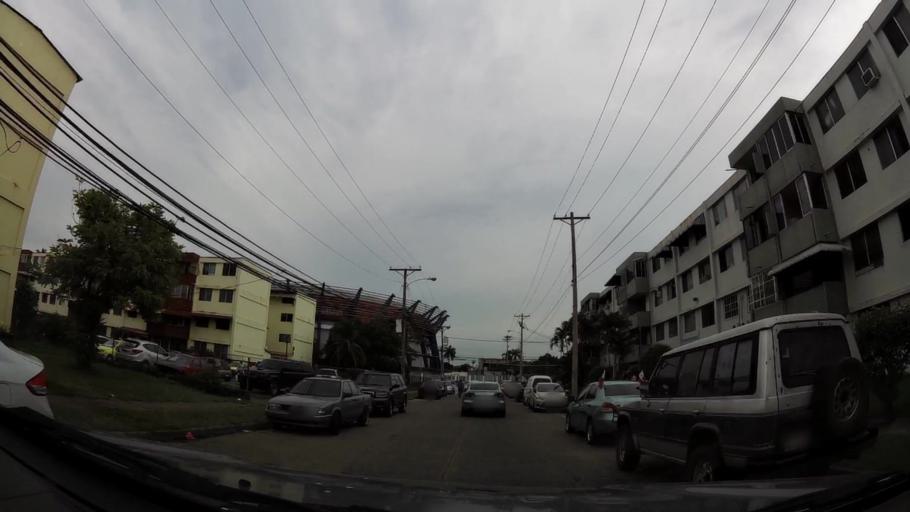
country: PA
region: Panama
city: San Miguelito
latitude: 9.0316
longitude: -79.4716
